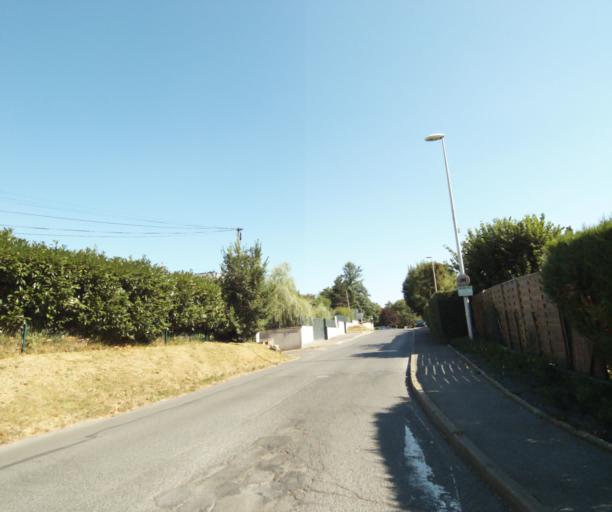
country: FR
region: Ile-de-France
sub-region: Departement de Seine-et-Marne
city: Gouvernes
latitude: 48.8657
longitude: 2.6982
